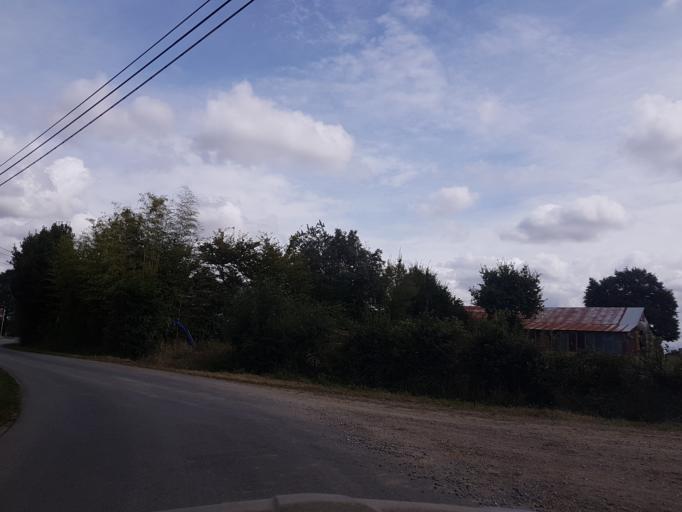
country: FR
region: Pays de la Loire
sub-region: Departement de la Loire-Atlantique
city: Les Touches
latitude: 47.4240
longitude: -1.4458
